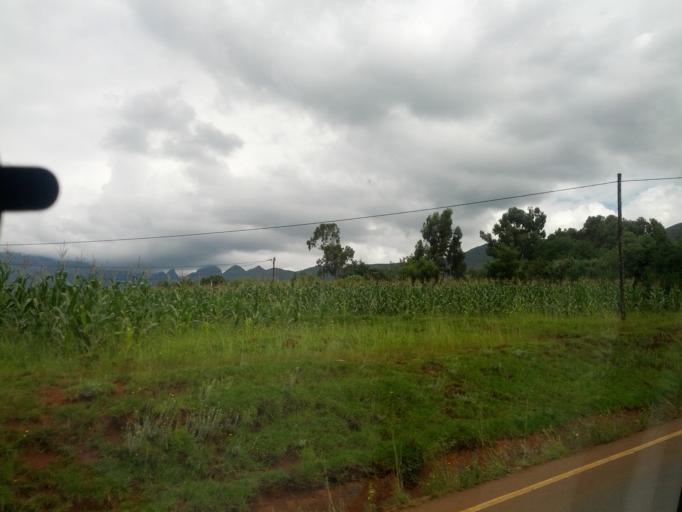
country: LS
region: Leribe
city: Leribe
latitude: -29.0391
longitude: 28.2449
